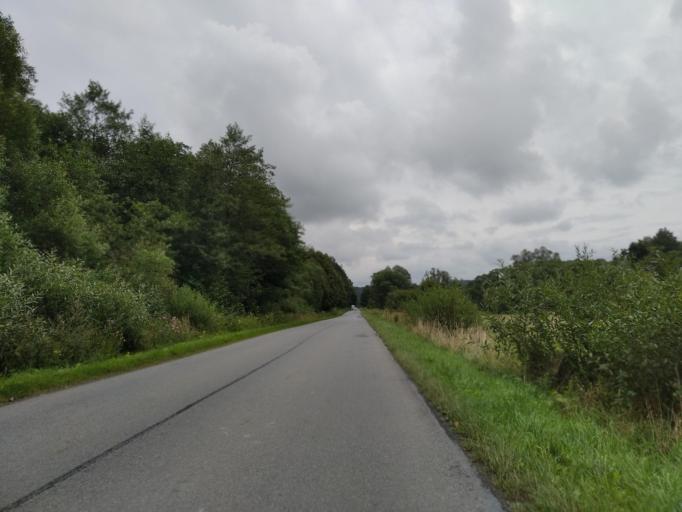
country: PL
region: Subcarpathian Voivodeship
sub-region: Powiat przemyski
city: Bircza
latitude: 49.6852
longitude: 22.4011
